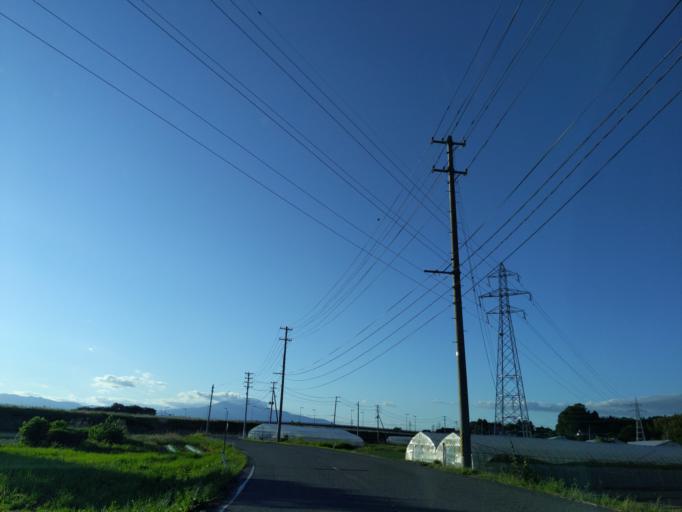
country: JP
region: Fukushima
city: Koriyama
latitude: 37.3912
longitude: 140.4122
